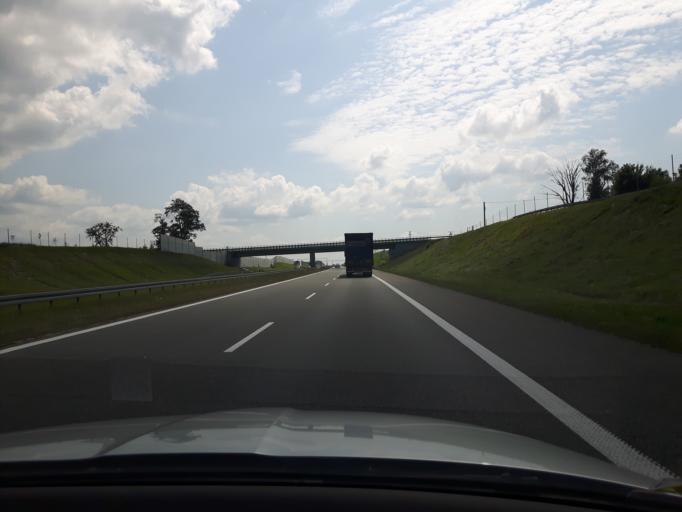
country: PL
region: Warmian-Masurian Voivodeship
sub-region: Powiat ostrodzki
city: Maldyty
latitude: 53.8750
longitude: 19.7379
